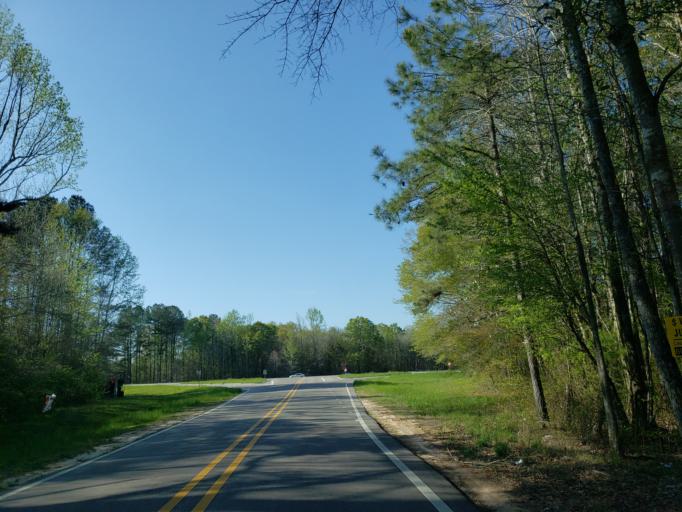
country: US
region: Mississippi
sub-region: Smith County
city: Taylorsville
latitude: 31.7037
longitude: -89.4155
